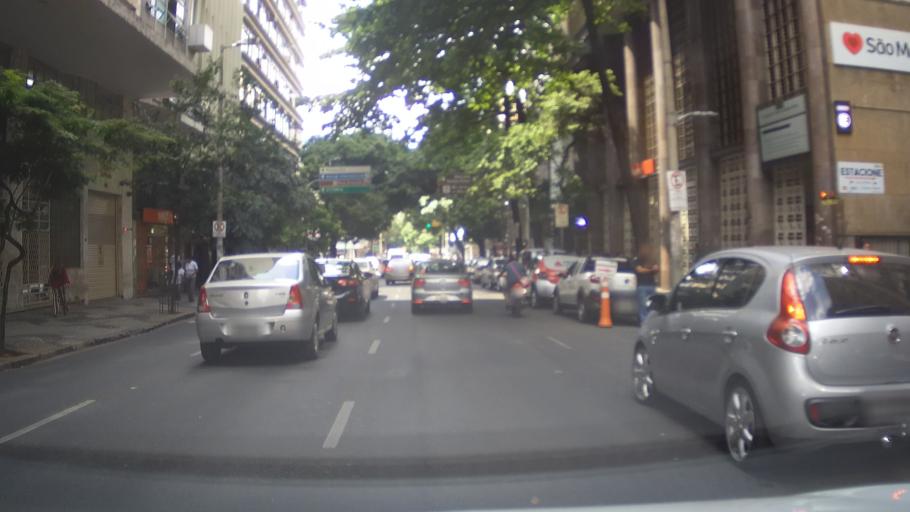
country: BR
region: Minas Gerais
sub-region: Belo Horizonte
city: Belo Horizonte
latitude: -19.9195
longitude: -43.9373
